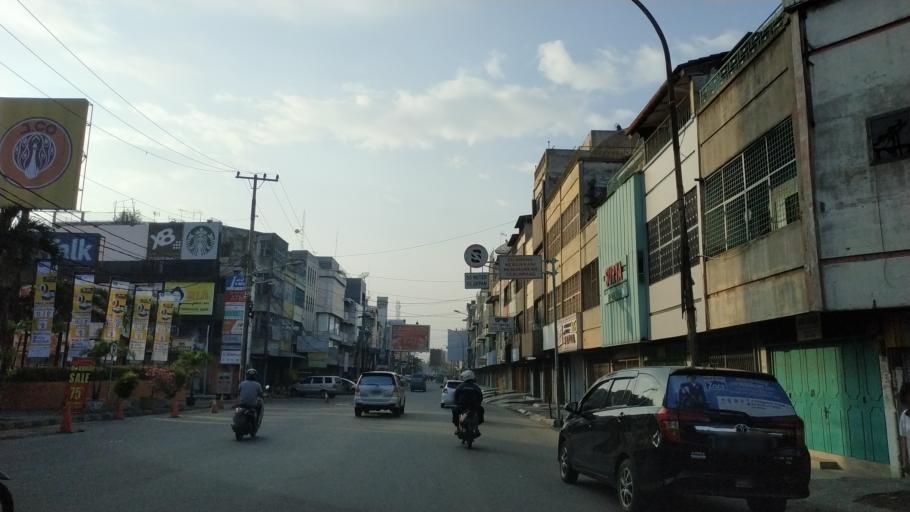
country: ID
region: North Sumatra
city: Medan
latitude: 3.5867
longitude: 98.6913
